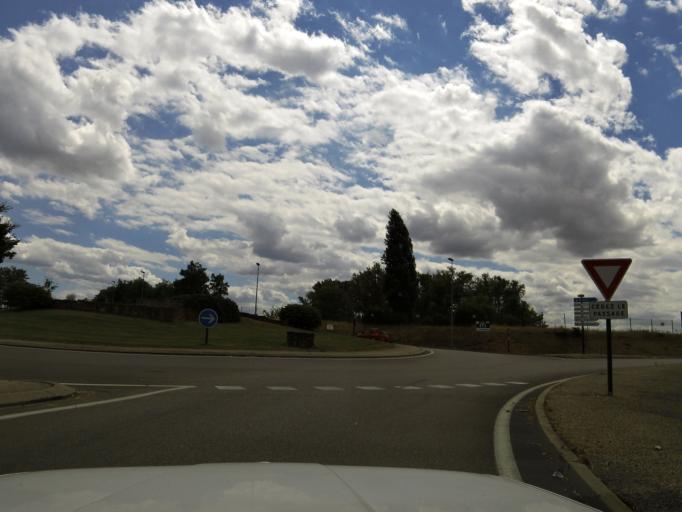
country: FR
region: Rhone-Alpes
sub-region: Departement de l'Ain
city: Loyettes
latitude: 45.7691
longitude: 5.2055
